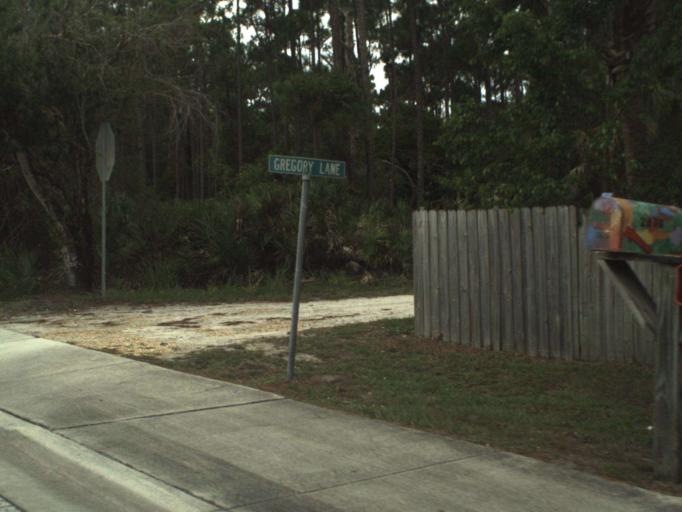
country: US
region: Florida
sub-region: Saint Lucie County
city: White City
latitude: 27.3688
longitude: -80.3504
